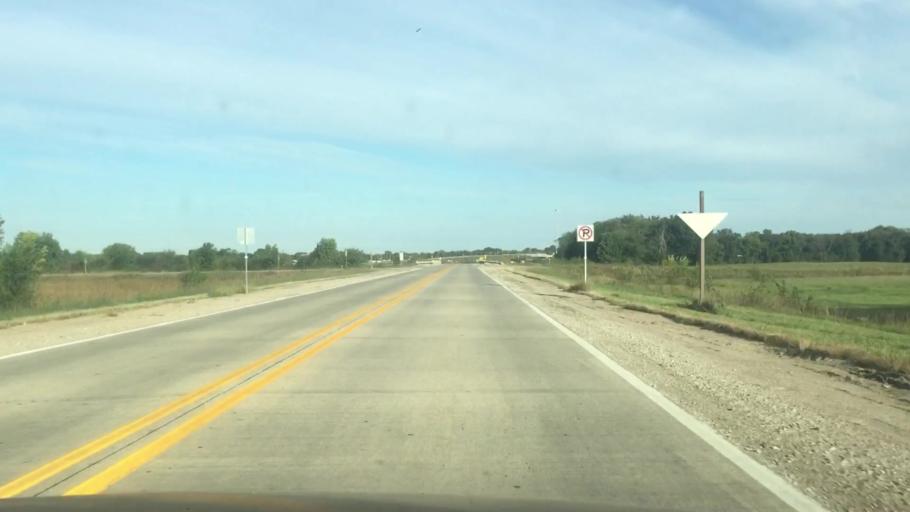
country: US
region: Nebraska
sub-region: Jefferson County
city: Fairbury
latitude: 40.1246
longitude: -97.1618
